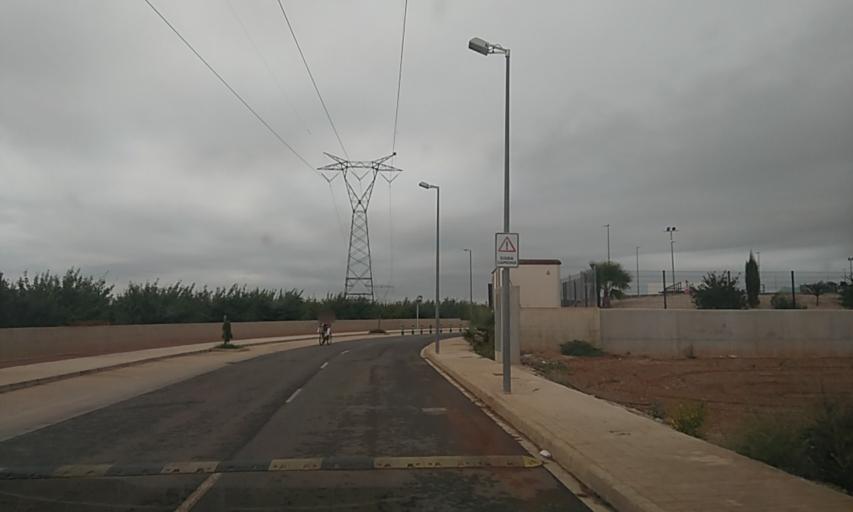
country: ES
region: Valencia
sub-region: Provincia de Valencia
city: L'Alcudia
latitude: 39.1928
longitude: -0.5171
